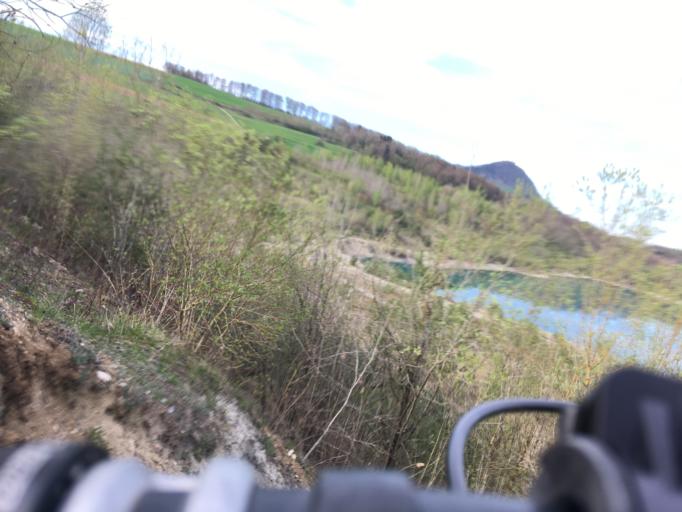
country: DE
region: Baden-Wuerttemberg
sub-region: Freiburg Region
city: Neuhausen
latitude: 47.8066
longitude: 8.7284
